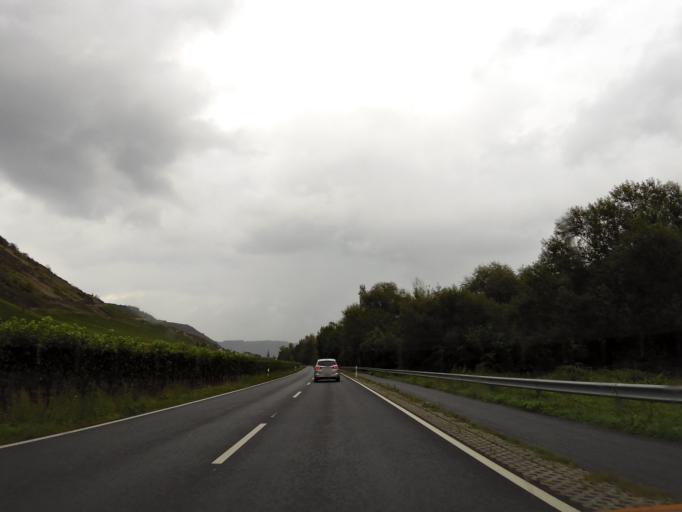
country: DE
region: Rheinland-Pfalz
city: Brieden
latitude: 50.1684
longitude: 7.2565
